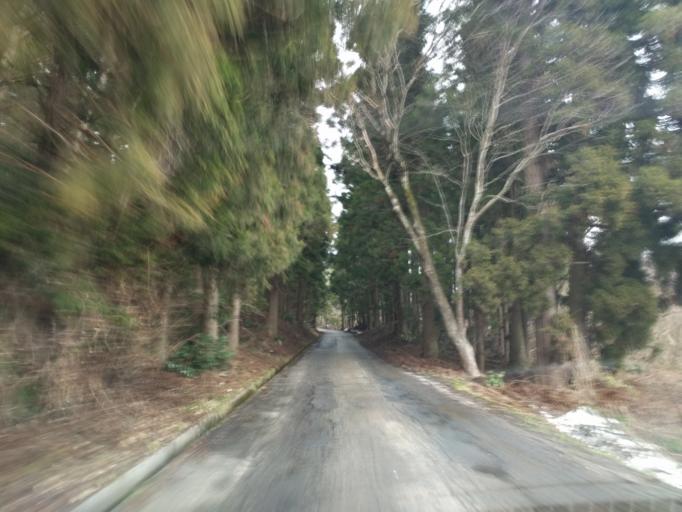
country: JP
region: Fukushima
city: Kitakata
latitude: 37.6749
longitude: 139.9193
